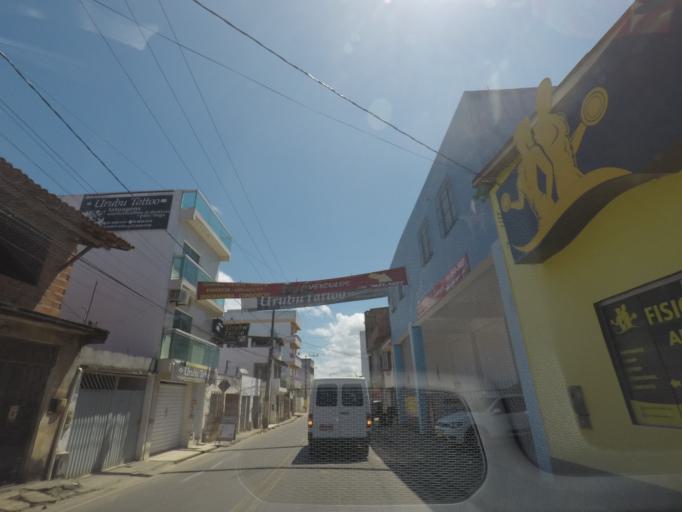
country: BR
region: Bahia
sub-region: Valenca
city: Valenca
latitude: -13.3747
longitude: -39.0732
